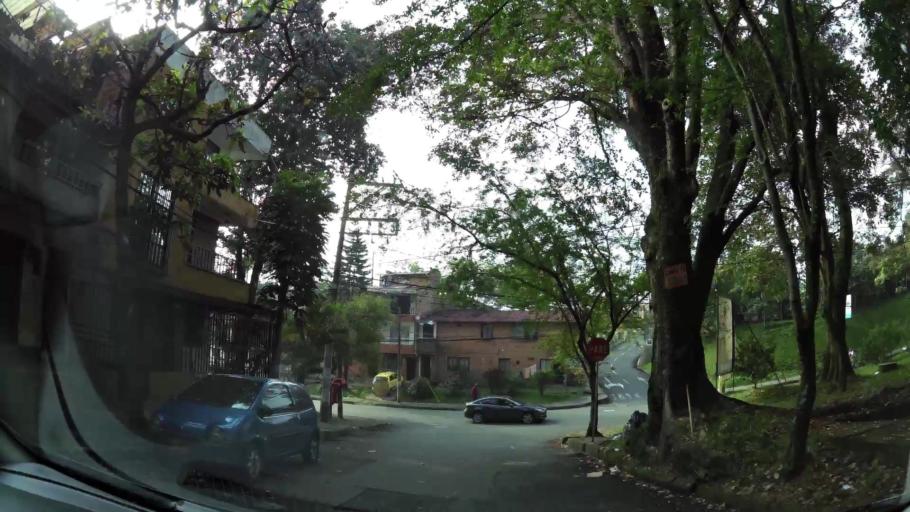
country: CO
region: Antioquia
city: Sabaneta
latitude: 6.1611
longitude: -75.6262
